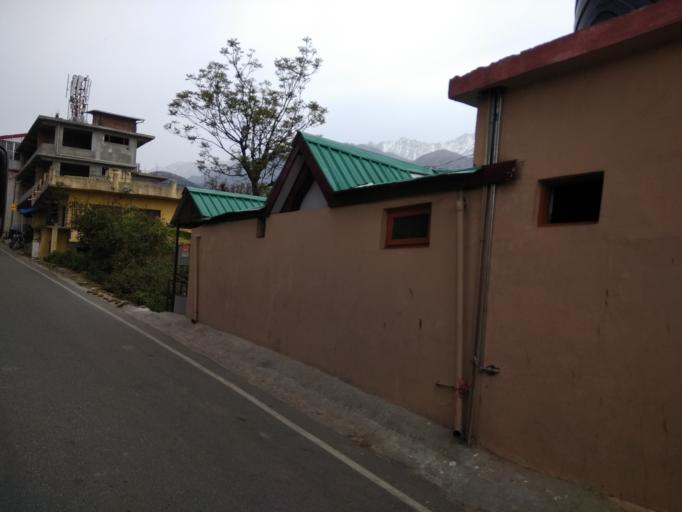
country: IN
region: Himachal Pradesh
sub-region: Kangra
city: Dharmsala
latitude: 32.2059
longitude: 76.3245
